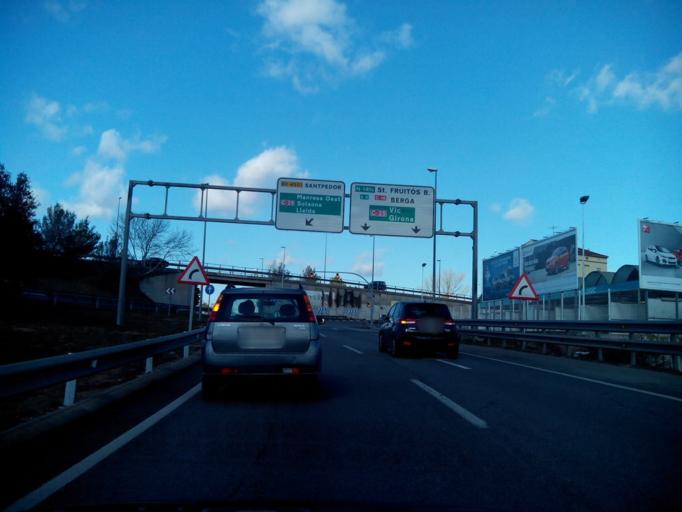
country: ES
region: Catalonia
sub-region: Provincia de Barcelona
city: Sant Fruitos de Bages
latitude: 41.7386
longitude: 1.8504
